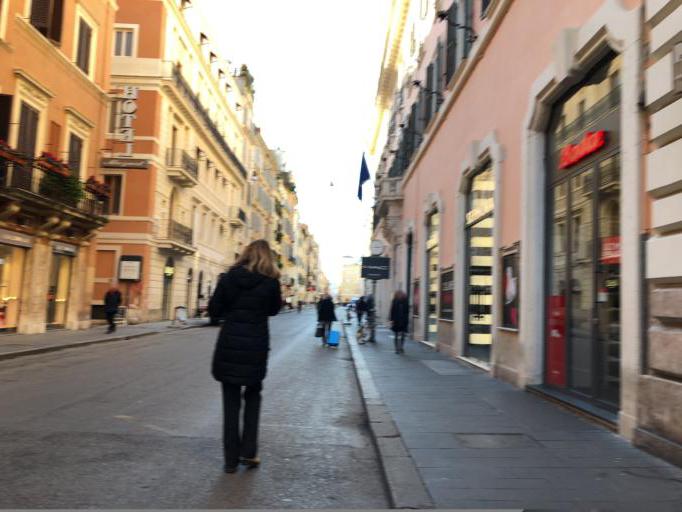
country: VA
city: Vatican City
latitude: 41.9074
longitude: 12.4777
